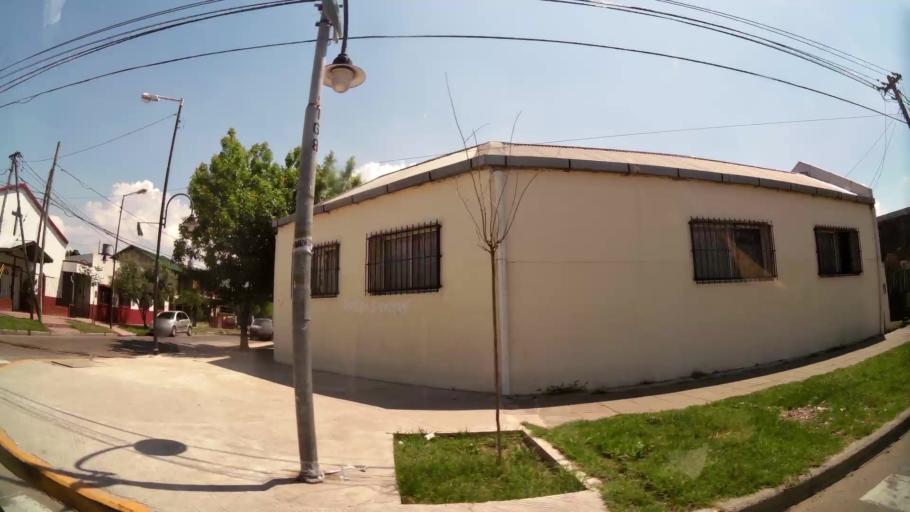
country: AR
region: Buenos Aires
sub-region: Partido de Tigre
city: Tigre
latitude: -34.4481
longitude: -58.5781
